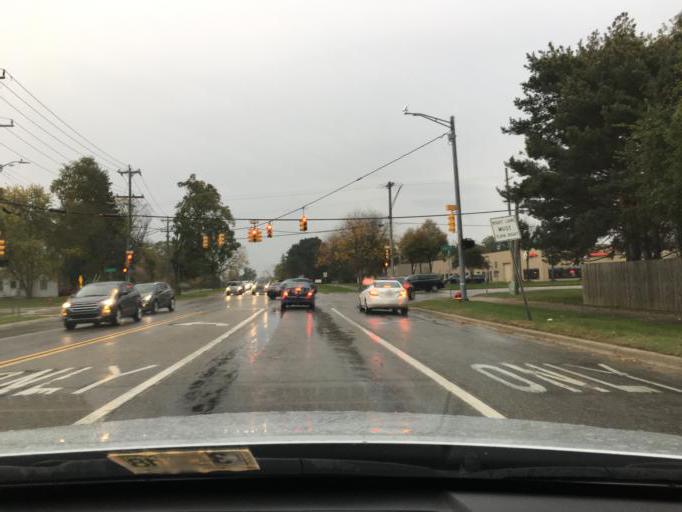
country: US
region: Michigan
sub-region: Oakland County
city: Rochester
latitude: 42.6667
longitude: -83.1138
